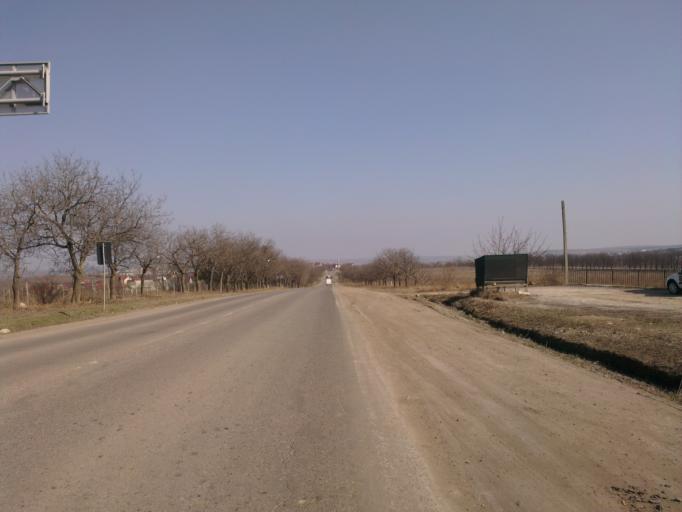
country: MD
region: Chisinau
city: Stauceni
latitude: 47.1161
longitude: 28.8622
